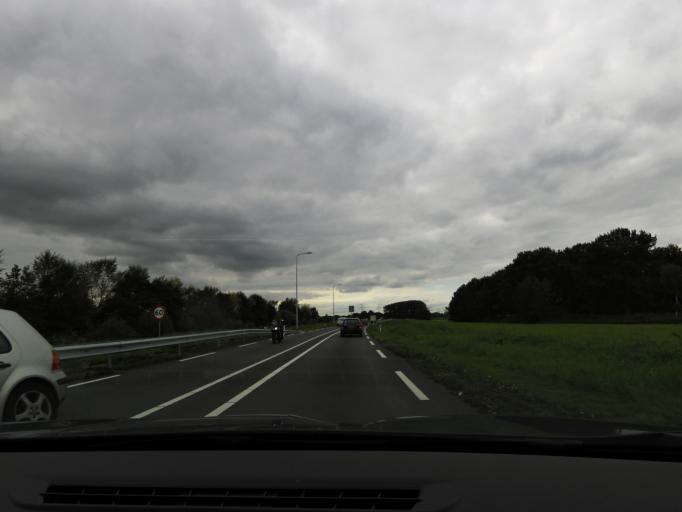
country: NL
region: South Holland
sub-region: Molenwaard
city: Nieuw-Lekkerland
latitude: 51.9153
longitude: 4.6605
